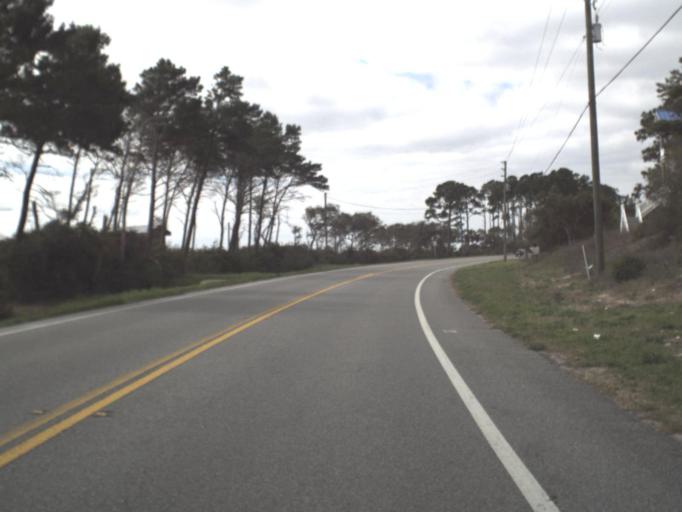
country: US
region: Florida
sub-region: Franklin County
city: Carrabelle
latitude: 29.8219
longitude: -84.7073
